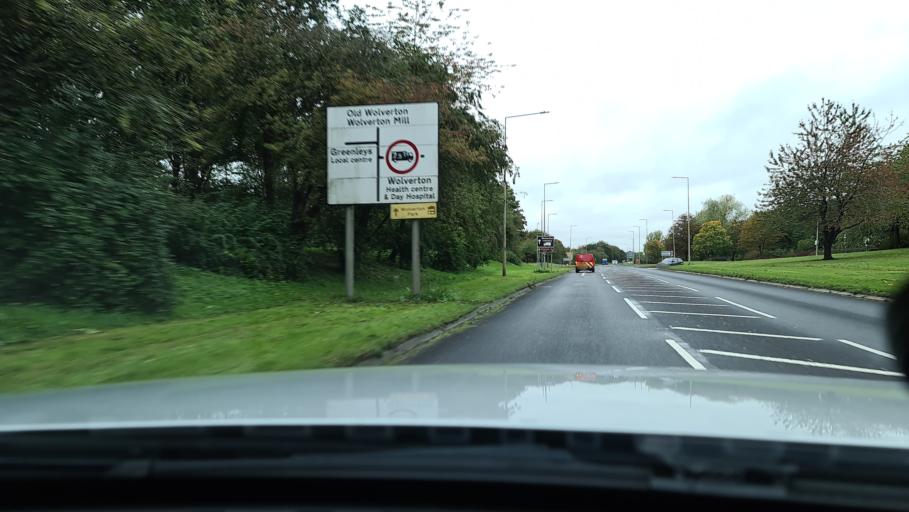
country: GB
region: England
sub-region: Milton Keynes
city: Bradwell
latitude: 52.0530
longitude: -0.8137
